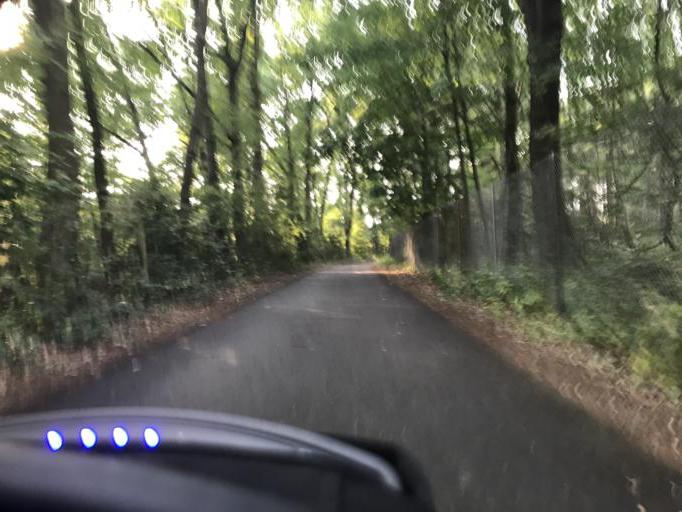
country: DE
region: North Rhine-Westphalia
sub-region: Regierungsbezirk Koln
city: Stossdorf
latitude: 50.7691
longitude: 7.2262
